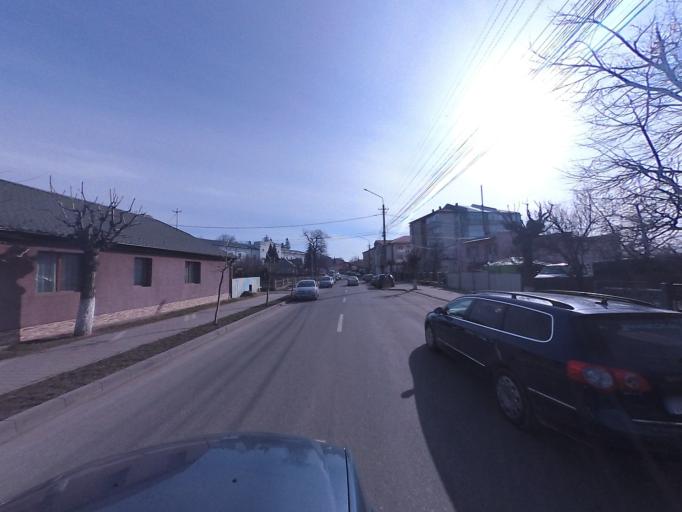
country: RO
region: Neamt
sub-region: Oras Targu Neamt
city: Humulesti
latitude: 47.2078
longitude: 26.3559
